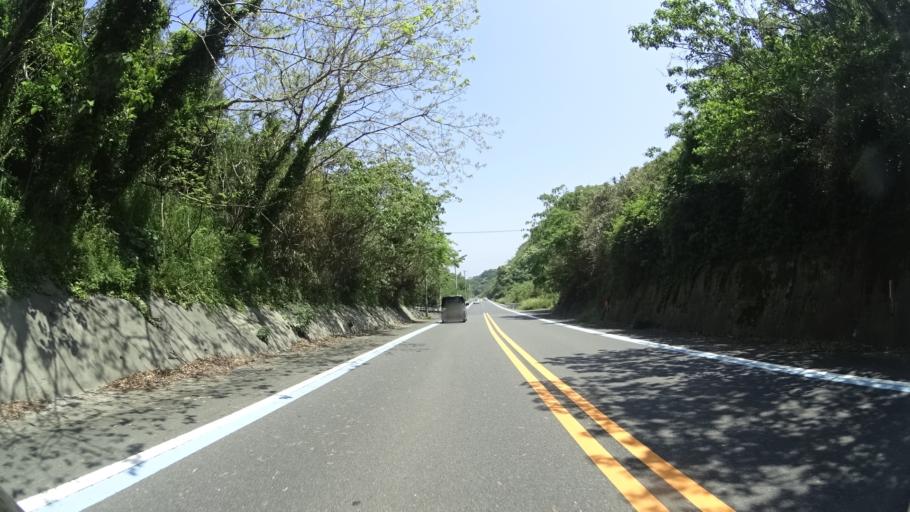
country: JP
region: Ehime
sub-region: Nishiuwa-gun
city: Ikata-cho
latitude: 33.5354
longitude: 132.3998
